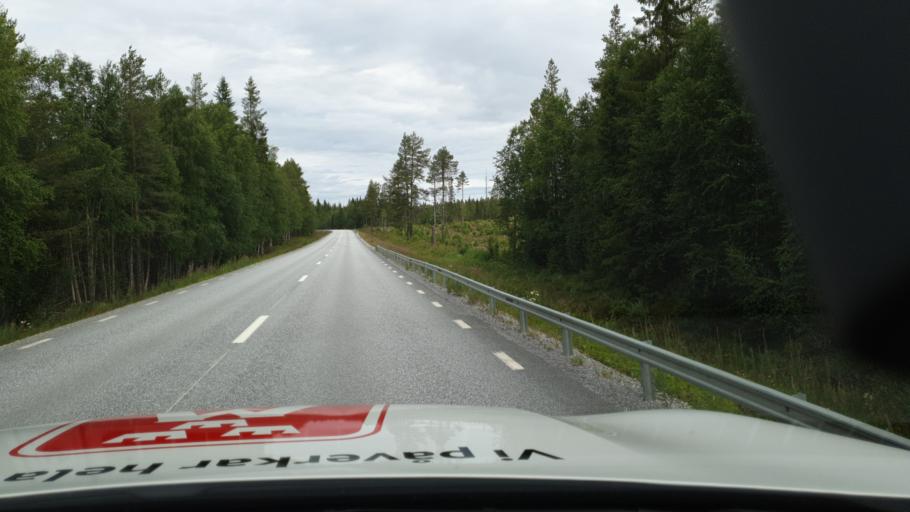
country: SE
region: Vaesterbotten
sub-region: Storumans Kommun
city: Storuman
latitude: 65.2107
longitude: 16.9898
